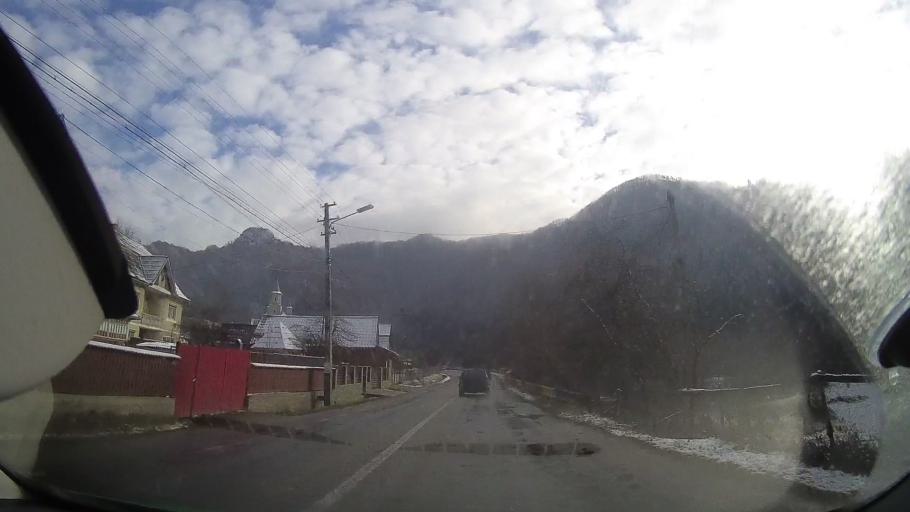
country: RO
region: Alba
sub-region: Oras Baia de Aries
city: Baia de Aries
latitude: 46.3901
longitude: 23.2921
